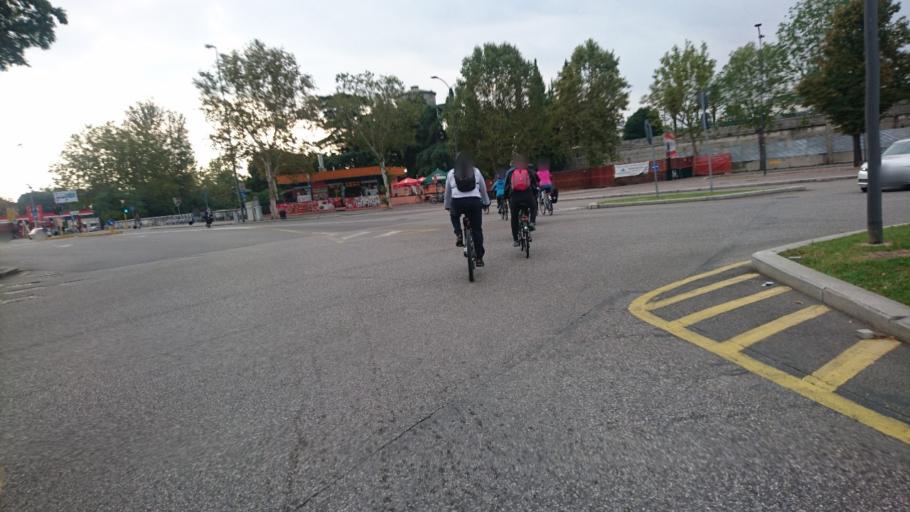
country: IT
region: Veneto
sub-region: Provincia di Verona
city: Verona
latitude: 45.4301
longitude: 10.9843
